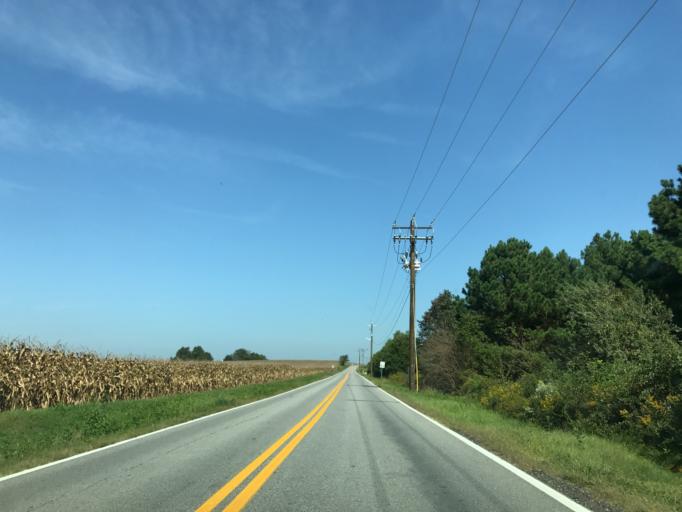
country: US
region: Maryland
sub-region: Queen Anne's County
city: Kingstown
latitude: 39.2578
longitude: -75.9438
